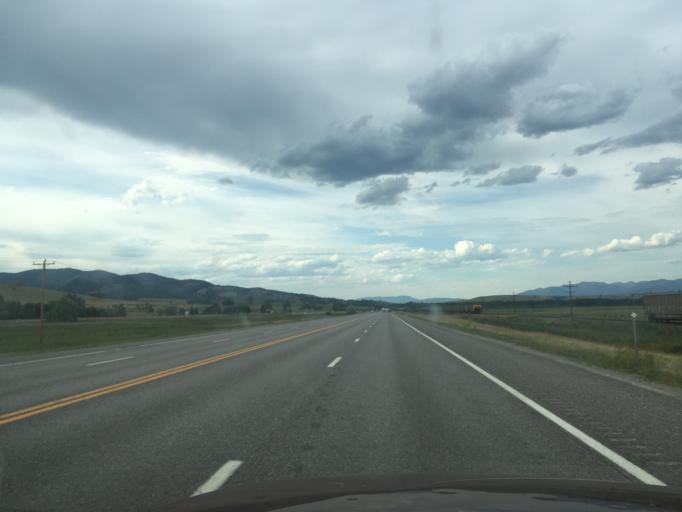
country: US
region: Montana
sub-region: Missoula County
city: Lolo
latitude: 46.7207
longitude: -114.0777
